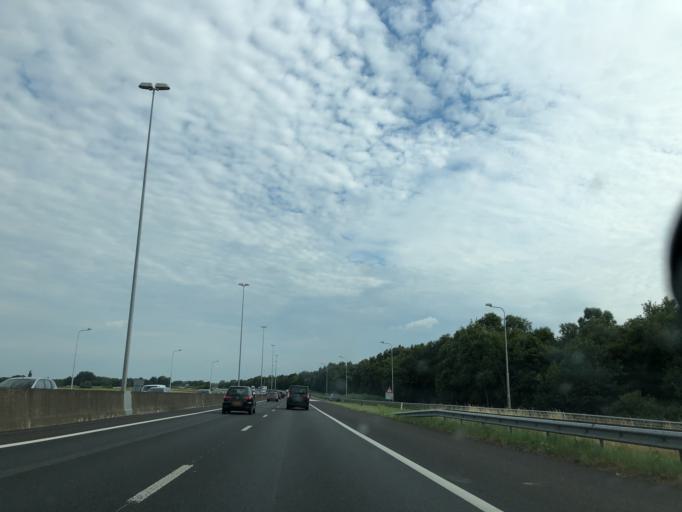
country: NL
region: Groningen
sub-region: Gemeente Haren
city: Haren
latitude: 53.1647
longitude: 6.5926
